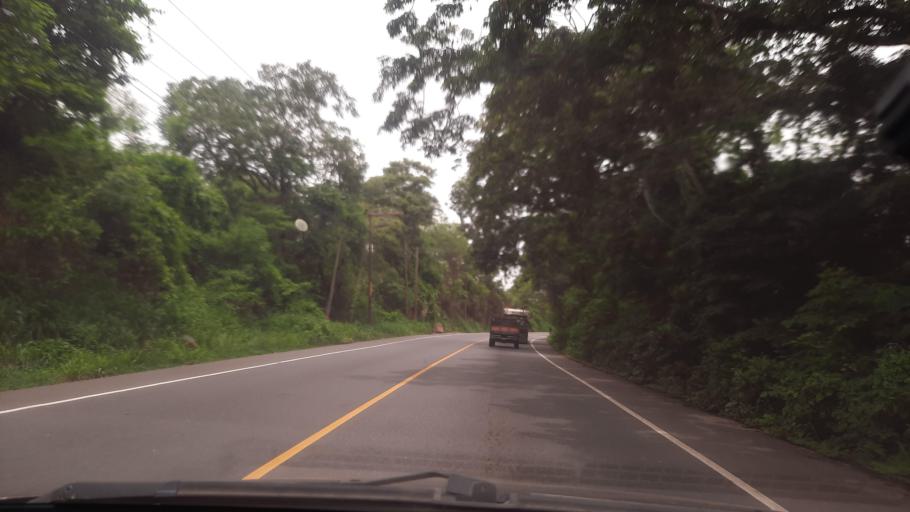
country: GT
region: Zacapa
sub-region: Municipio de Zacapa
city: Gualan
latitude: 15.1472
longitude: -89.3269
